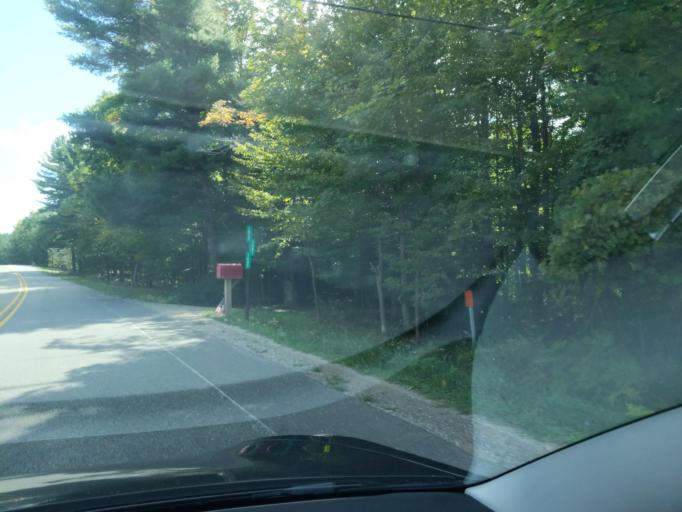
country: US
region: Michigan
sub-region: Antrim County
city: Bellaire
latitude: 45.0572
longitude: -85.3190
